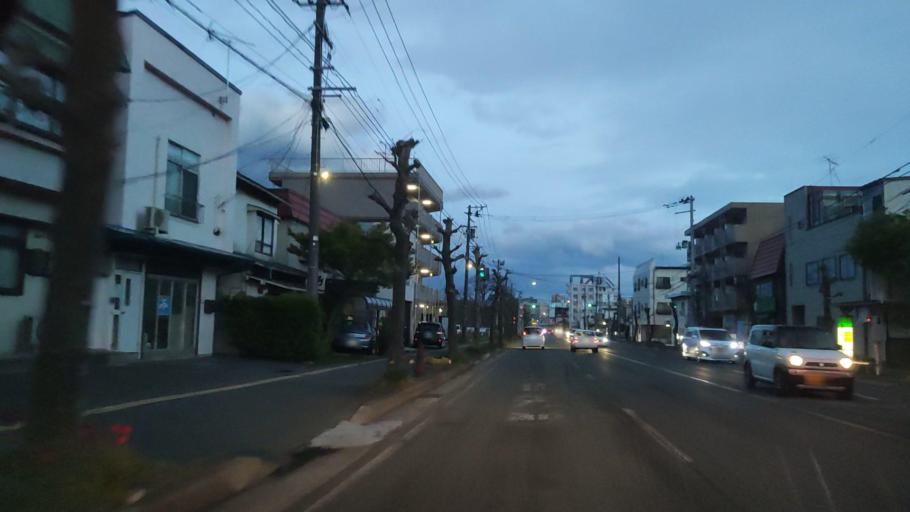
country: JP
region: Iwate
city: Morioka-shi
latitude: 39.7142
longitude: 141.1298
